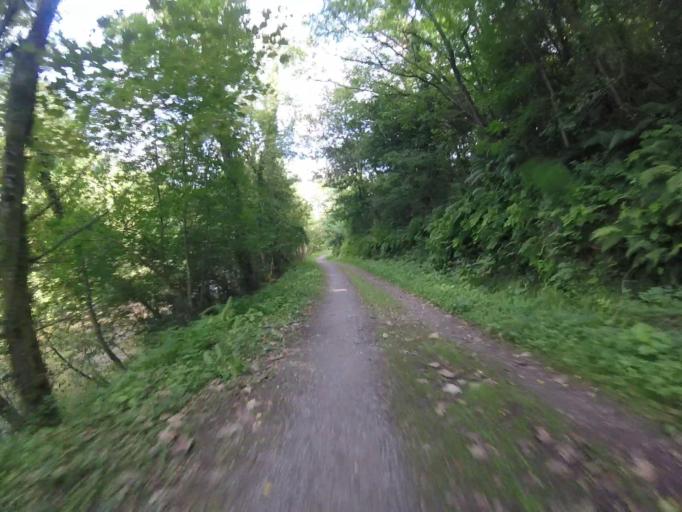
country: ES
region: Basque Country
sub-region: Provincia de Guipuzcoa
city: Hernani
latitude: 43.2459
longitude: -1.9512
